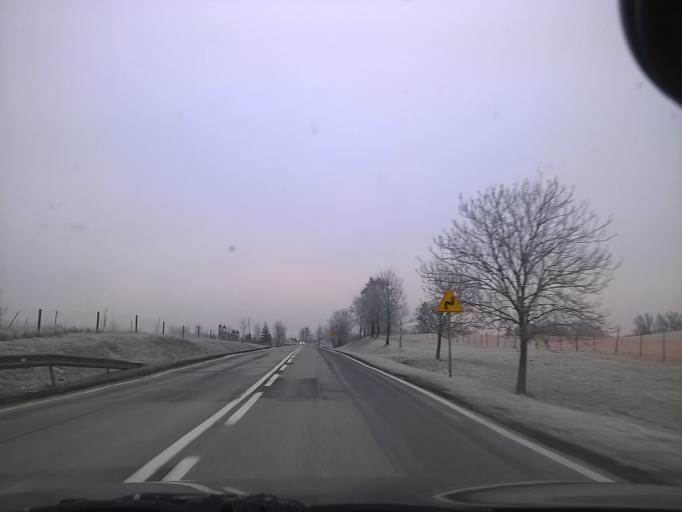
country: PL
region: Warmian-Masurian Voivodeship
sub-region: Powiat mragowski
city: Mragowo
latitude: 53.8376
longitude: 21.1999
